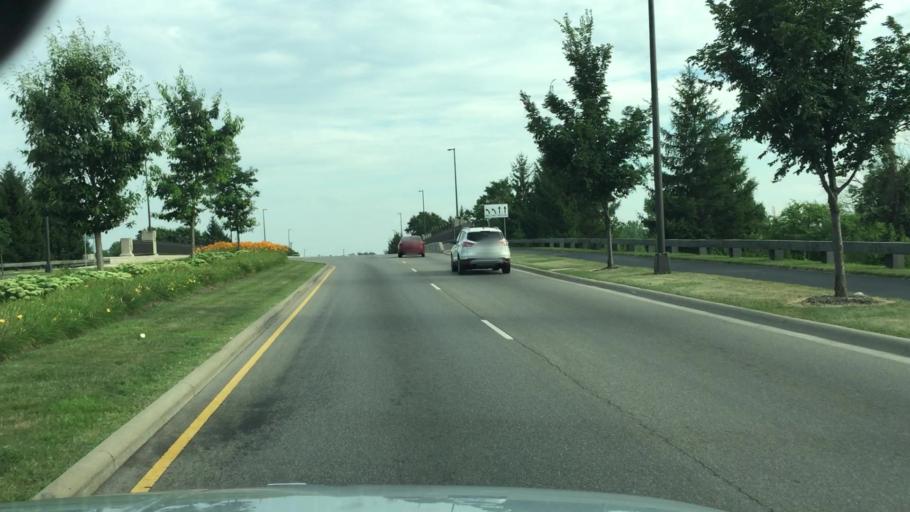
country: US
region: Ohio
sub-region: Franklin County
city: Dublin
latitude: 40.1003
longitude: -83.1591
